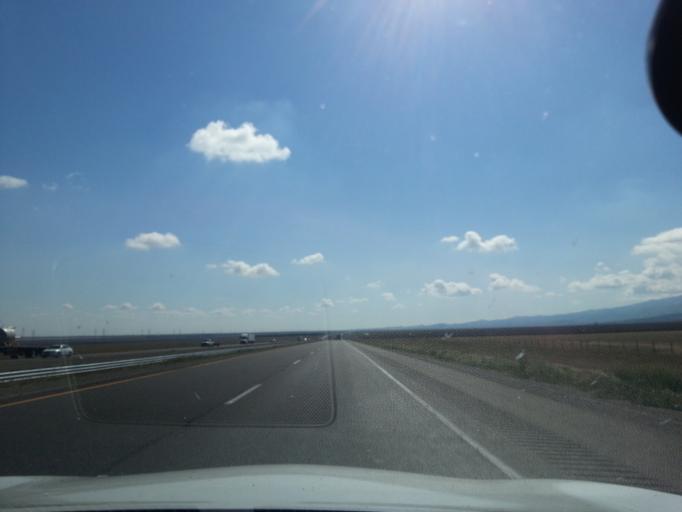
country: US
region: California
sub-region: Fresno County
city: San Joaquin
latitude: 36.4625
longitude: -120.4191
